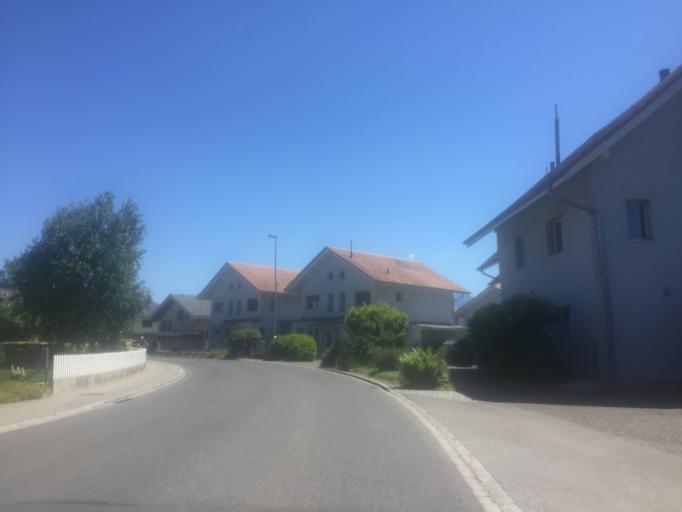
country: CH
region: Bern
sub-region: Thun District
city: Thierachern
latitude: 46.7527
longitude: 7.5783
